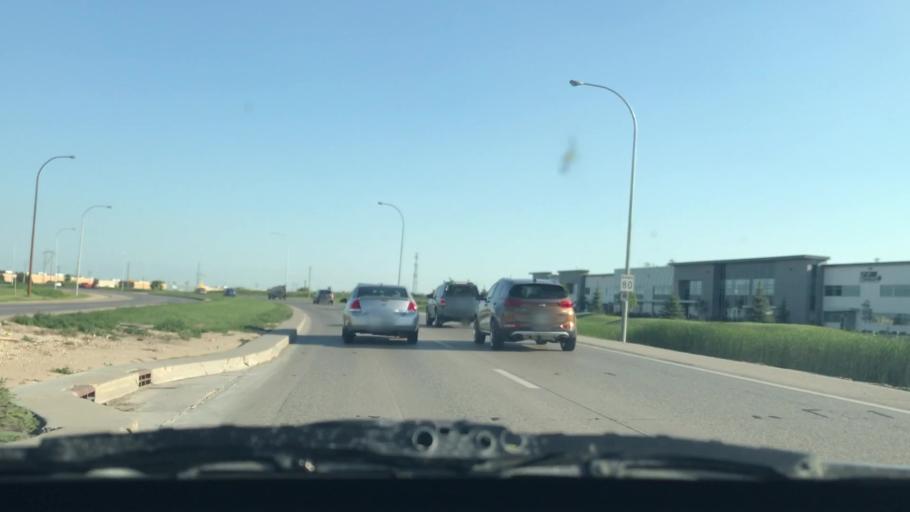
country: CA
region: Manitoba
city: Winnipeg
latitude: 49.8311
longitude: -97.2098
